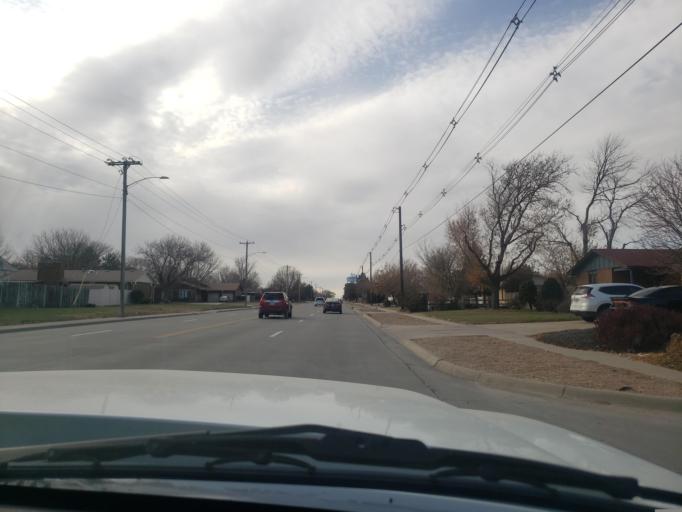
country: US
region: Kansas
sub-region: Finney County
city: Garden City
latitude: 37.9895
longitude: -100.8564
